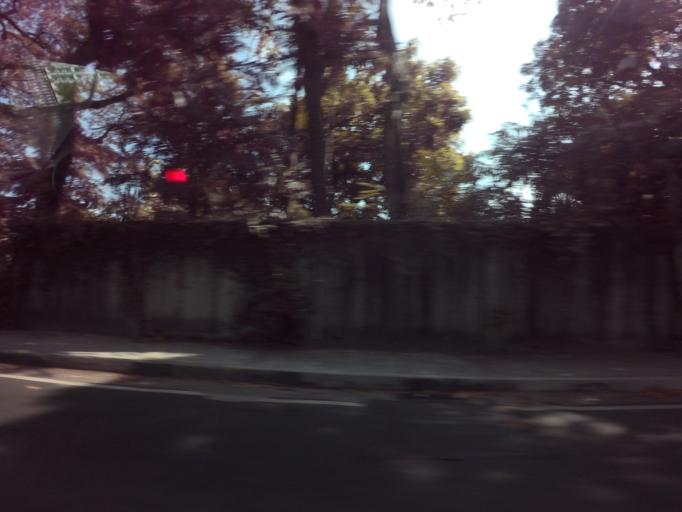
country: PH
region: Metro Manila
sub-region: Makati City
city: Makati City
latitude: 14.5449
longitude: 121.0437
